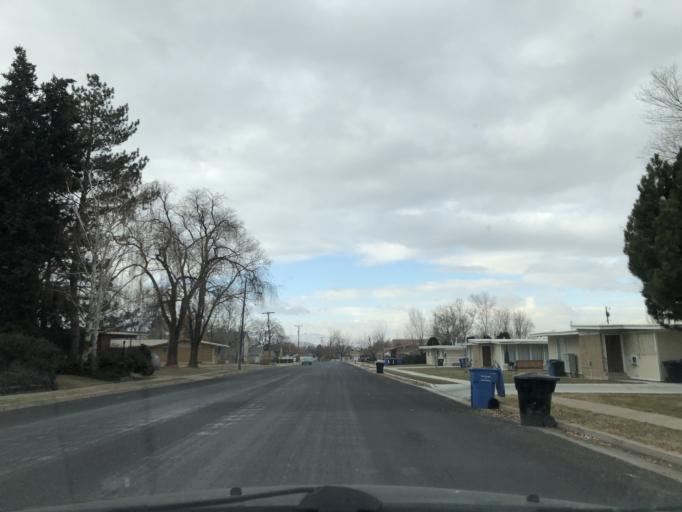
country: US
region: Utah
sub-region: Cache County
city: Logan
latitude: 41.7465
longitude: -111.8369
